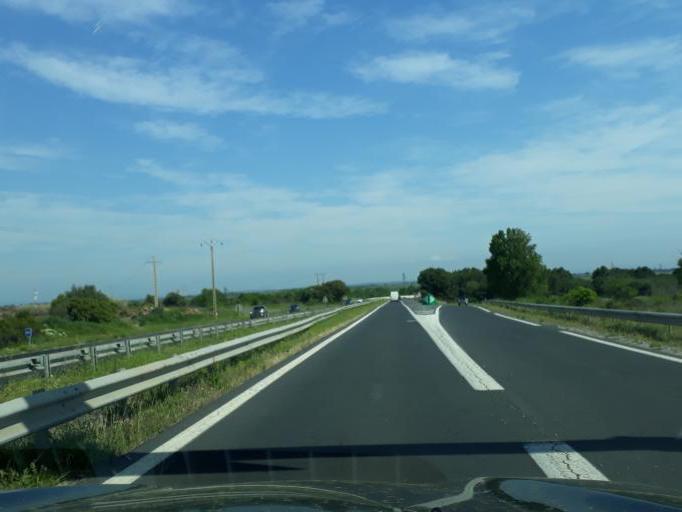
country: FR
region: Languedoc-Roussillon
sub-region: Departement de l'Herault
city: Le Cap d'Agde
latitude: 43.3049
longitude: 3.5079
